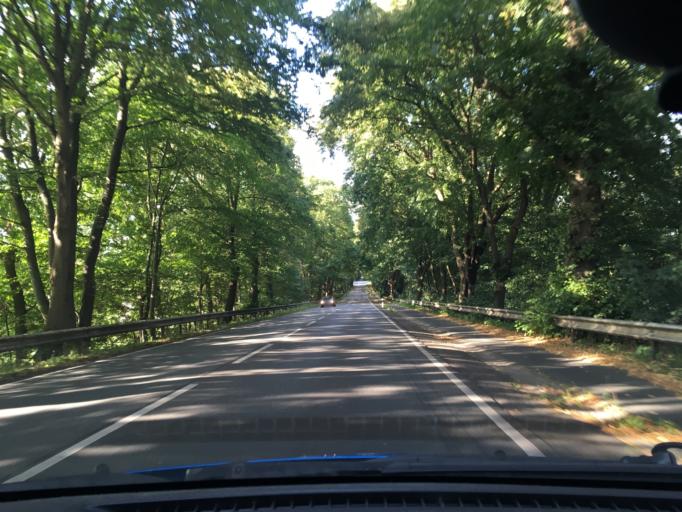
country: DE
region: Lower Saxony
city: Seevetal
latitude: 53.4073
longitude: 9.9256
